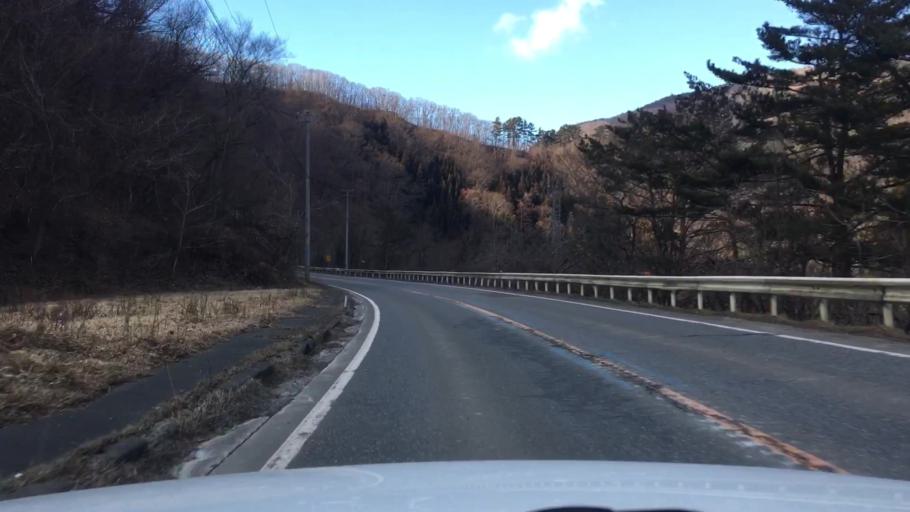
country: JP
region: Iwate
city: Tono
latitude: 39.6193
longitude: 141.6225
